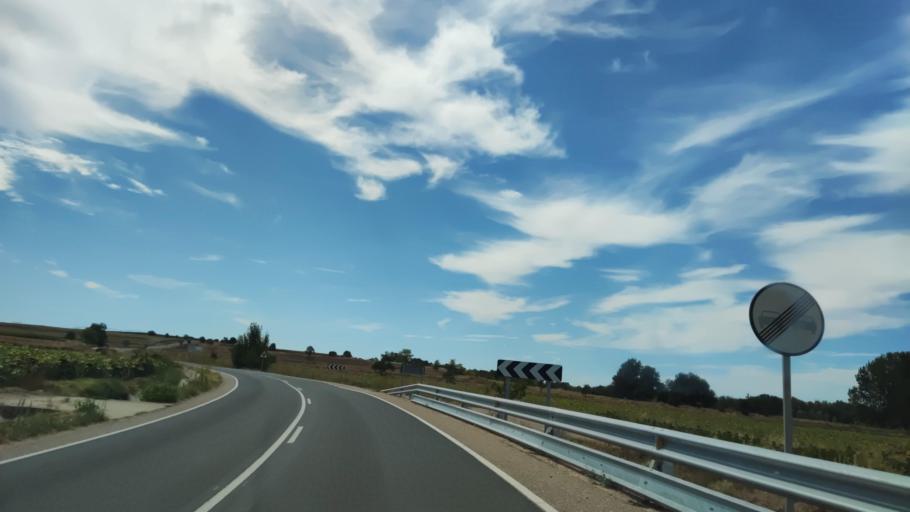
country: ES
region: Castille and Leon
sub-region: Provincia de Zamora
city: Villalazan
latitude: 41.4958
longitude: -5.5954
